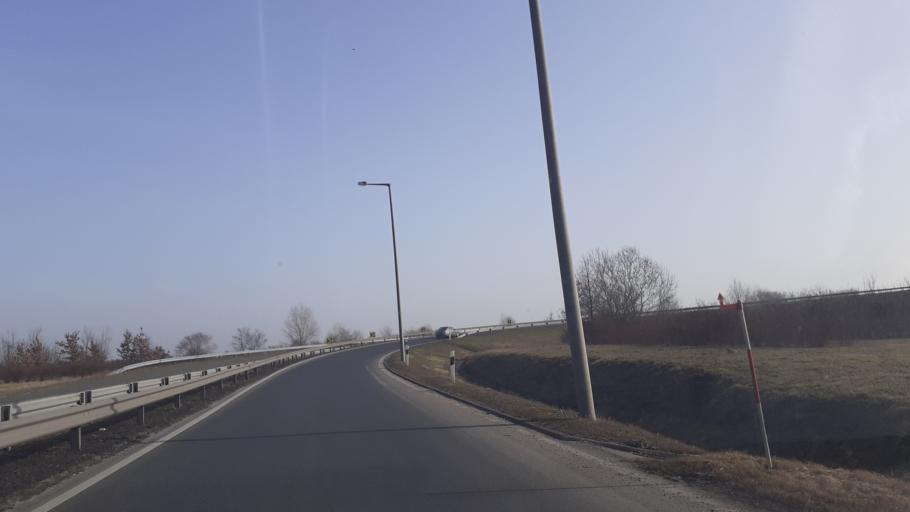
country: HU
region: Bacs-Kiskun
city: Dunavecse
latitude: 46.8983
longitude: 18.9867
